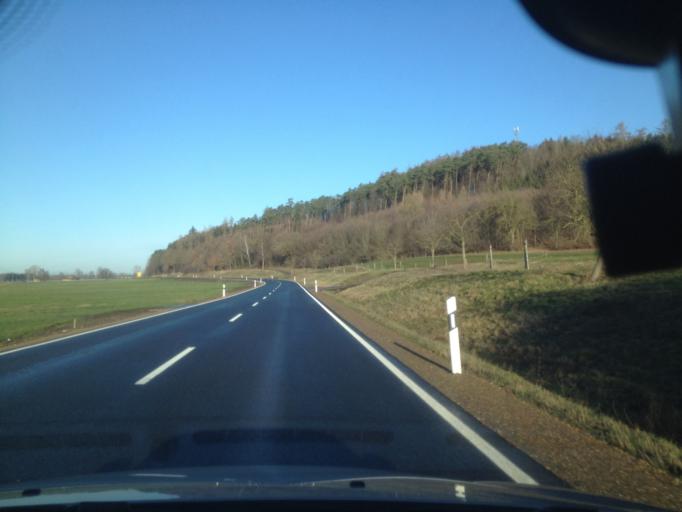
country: DE
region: Bavaria
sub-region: Swabia
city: Haldenwang
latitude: 48.4379
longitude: 10.4341
